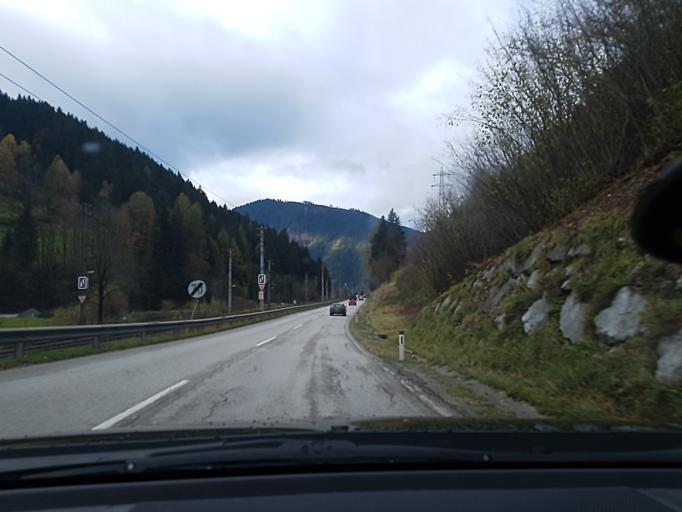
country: AT
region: Styria
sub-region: Politischer Bezirk Liezen
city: Selzthal
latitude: 47.5391
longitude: 14.3085
